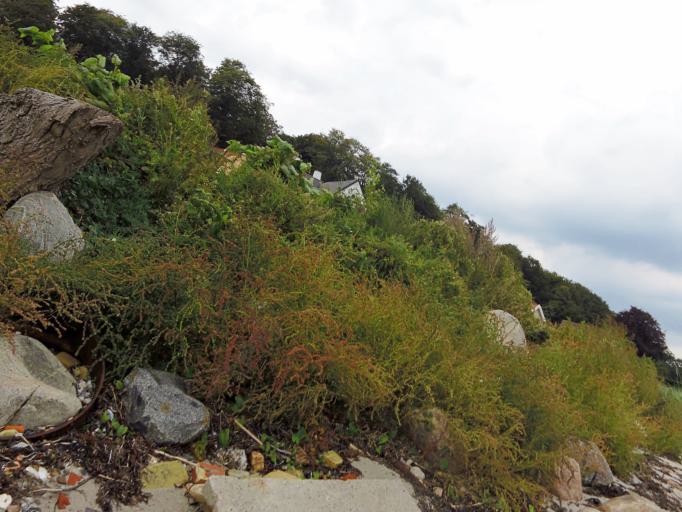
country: DK
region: Capital Region
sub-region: Fredensborg Kommune
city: Humlebaek
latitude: 55.9464
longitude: 12.5297
